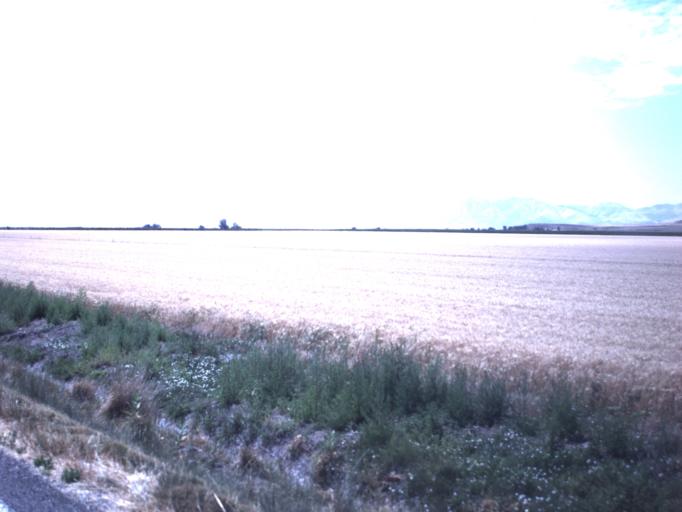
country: US
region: Utah
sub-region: Box Elder County
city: Tremonton
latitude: 41.6414
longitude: -112.3141
